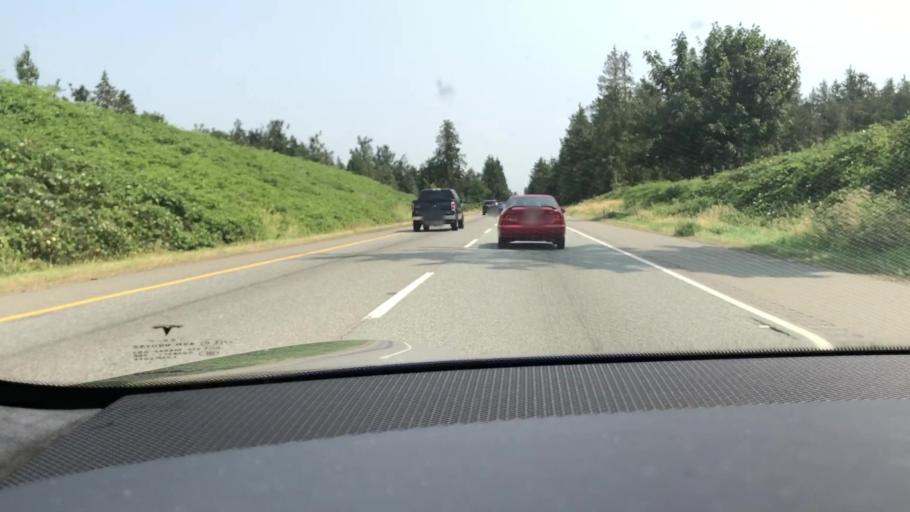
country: CA
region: British Columbia
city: Aldergrove
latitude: 49.0779
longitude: -122.4333
